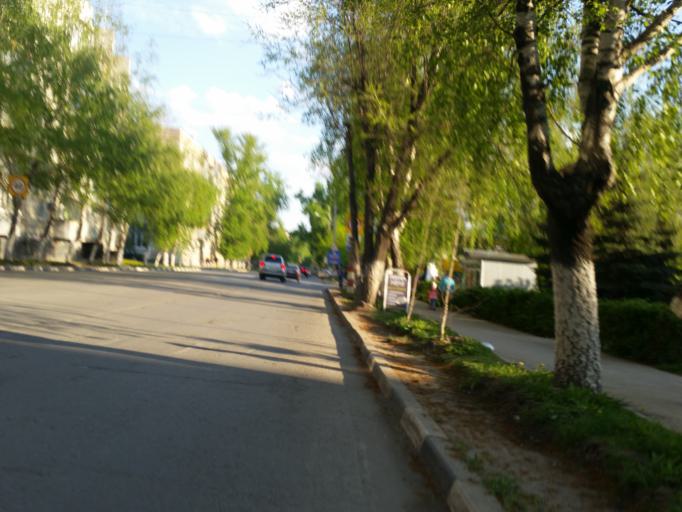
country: RU
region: Ulyanovsk
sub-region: Ulyanovskiy Rayon
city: Ulyanovsk
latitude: 54.3314
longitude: 48.3872
